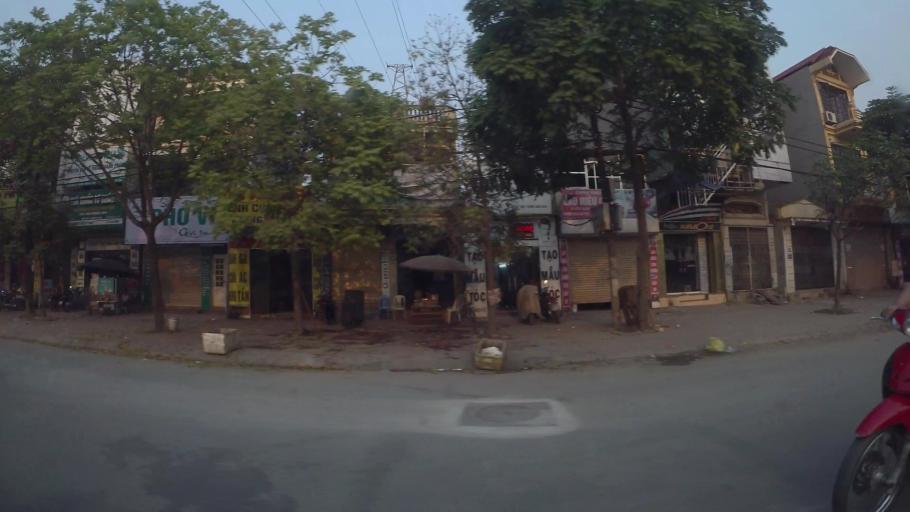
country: VN
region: Ha Noi
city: Van Dien
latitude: 20.9423
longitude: 105.8441
